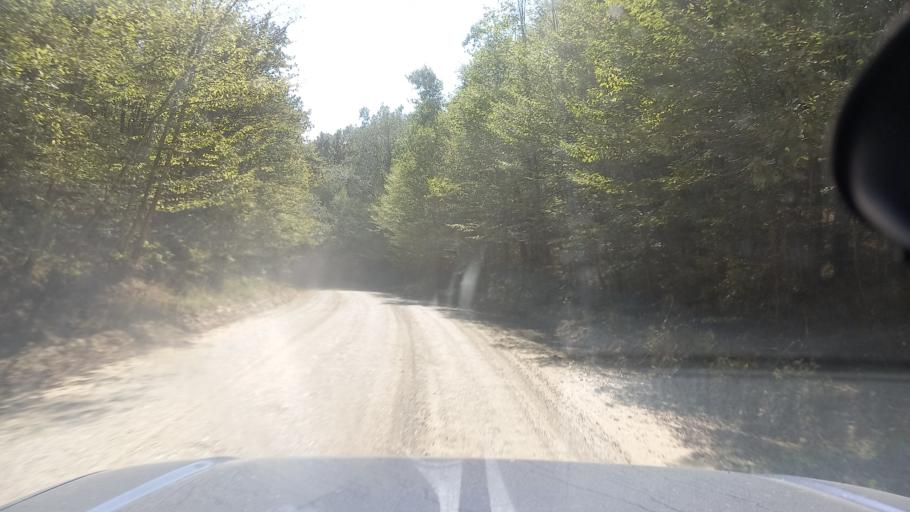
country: RU
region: Krasnodarskiy
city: Azovskaya
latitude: 44.6779
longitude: 38.6336
